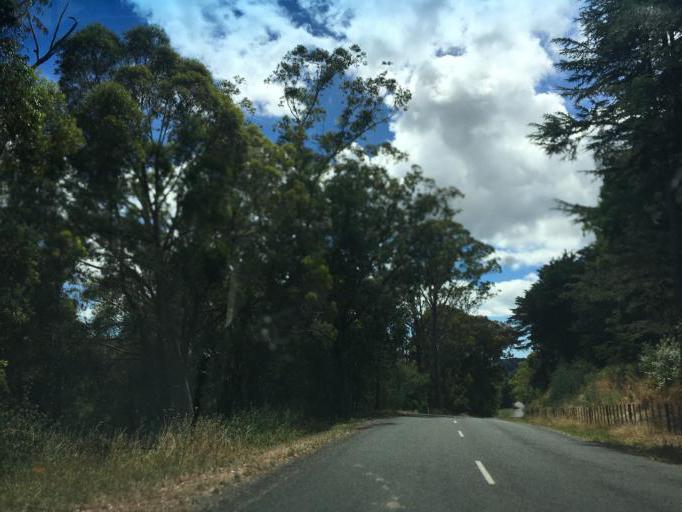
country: NZ
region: Hawke's Bay
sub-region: Hastings District
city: Hastings
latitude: -39.7548
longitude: 176.8669
